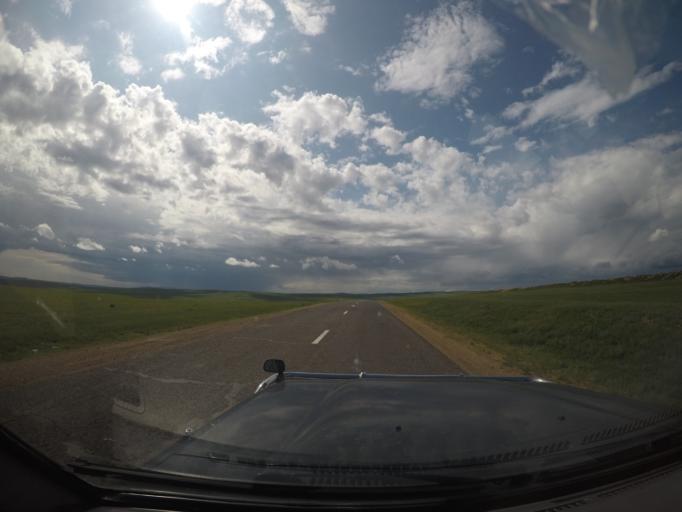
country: MN
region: Hentiy
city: Bayanbulag
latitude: 47.4599
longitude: 109.6416
